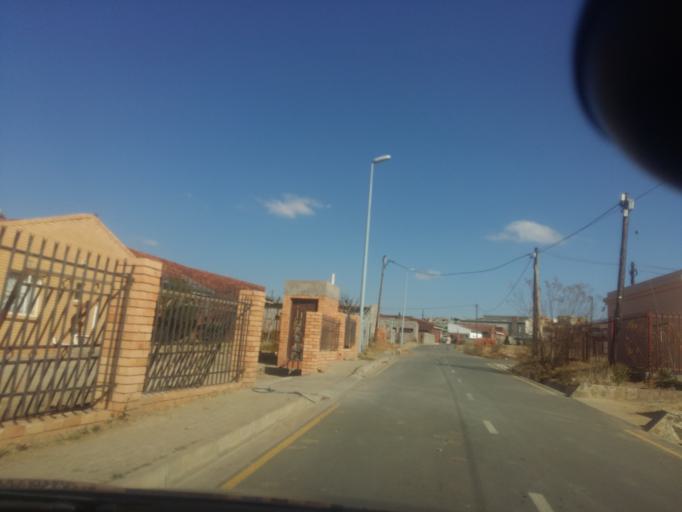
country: LS
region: Maseru
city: Maseru
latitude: -29.3413
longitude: 27.4519
